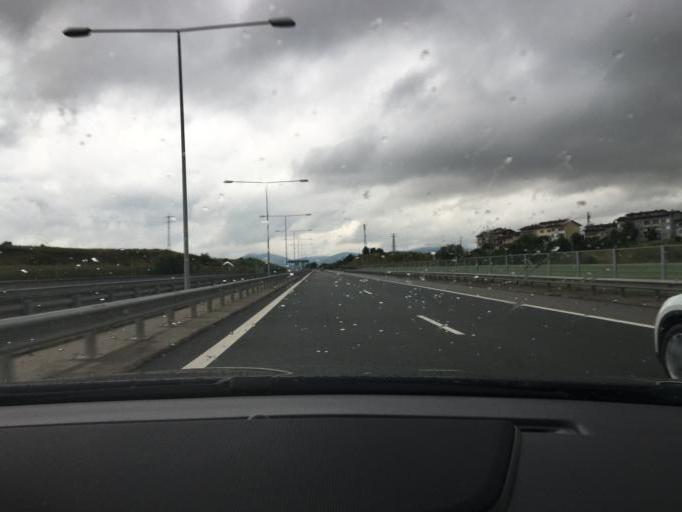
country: BG
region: Pernik
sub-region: Obshtina Pernik
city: Pernik
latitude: 42.5990
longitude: 23.1230
